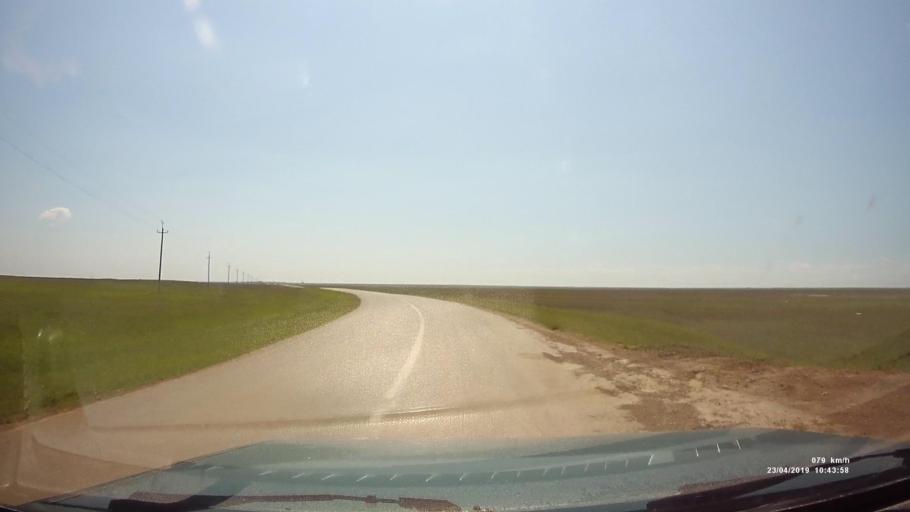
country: RU
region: Kalmykiya
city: Yashalta
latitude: 46.4636
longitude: 42.6508
